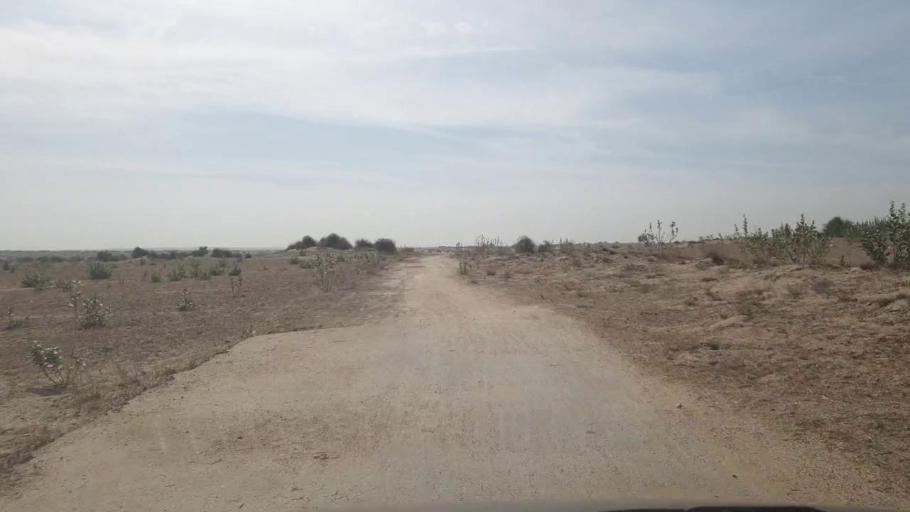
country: PK
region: Sindh
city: Umarkot
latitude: 25.2729
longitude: 69.7316
